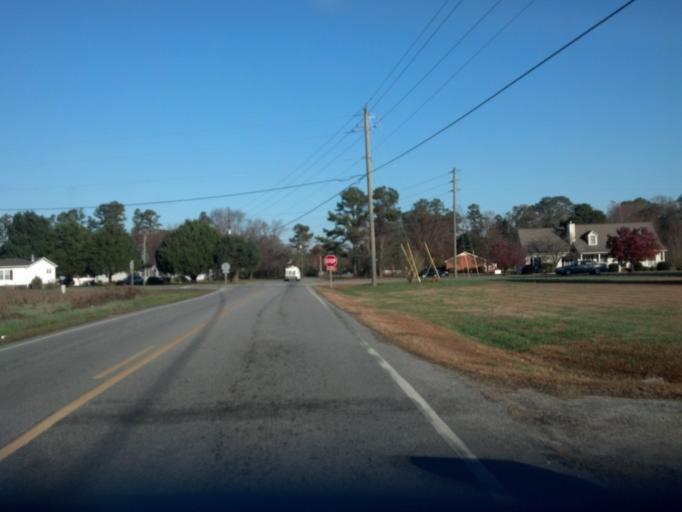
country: US
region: North Carolina
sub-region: Pitt County
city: Winterville
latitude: 35.5284
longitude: -77.4424
